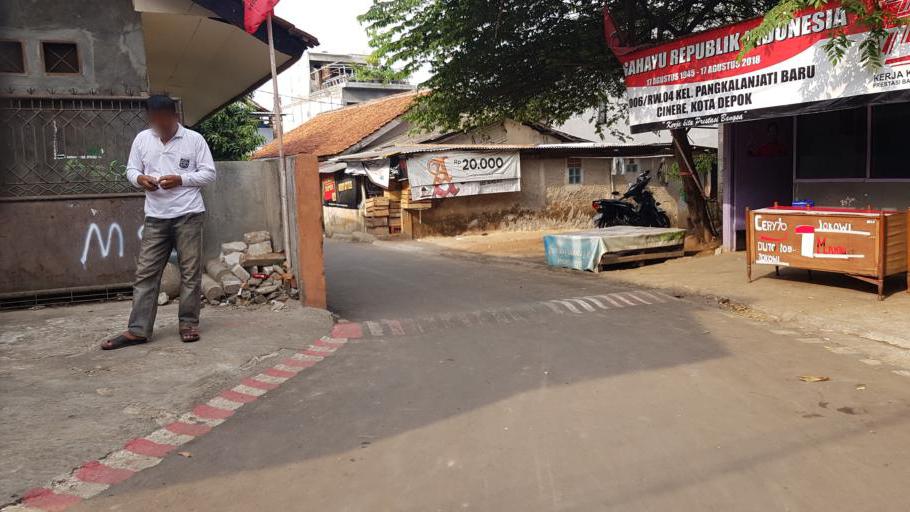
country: ID
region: West Java
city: Pamulang
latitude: -6.3270
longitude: 106.7981
